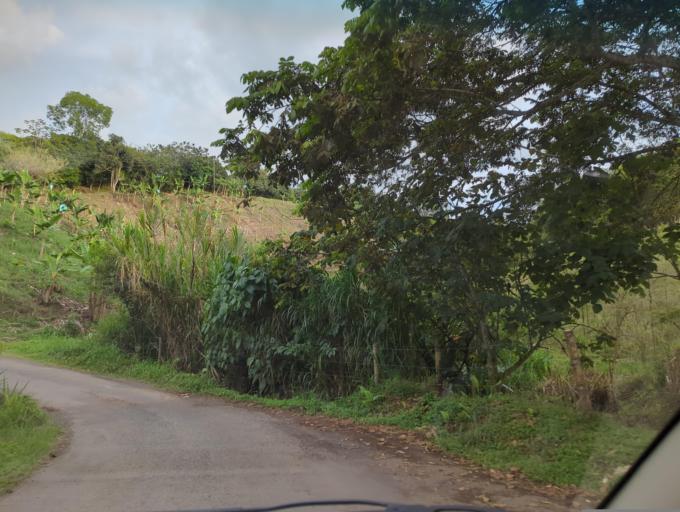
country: CO
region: Risaralda
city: Pereira
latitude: 4.8257
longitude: -75.7589
